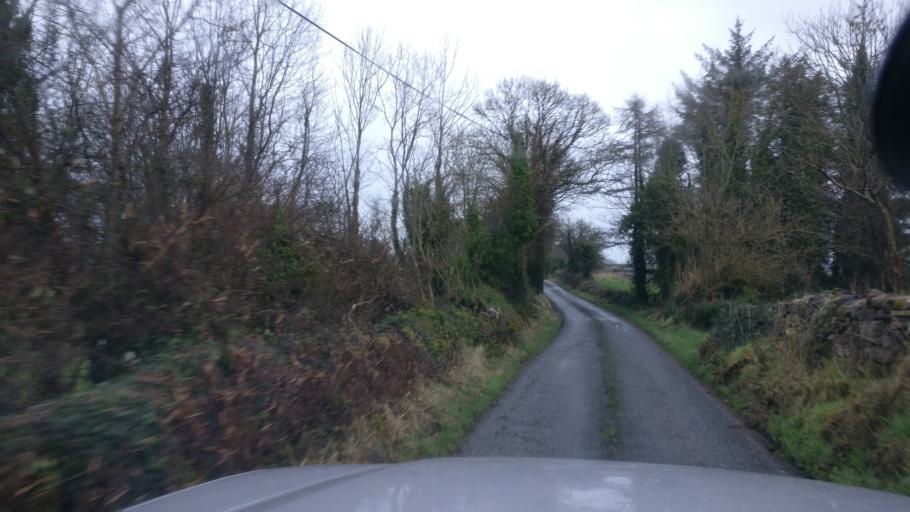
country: IE
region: Connaught
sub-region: County Galway
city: Loughrea
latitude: 53.1756
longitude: -8.6117
